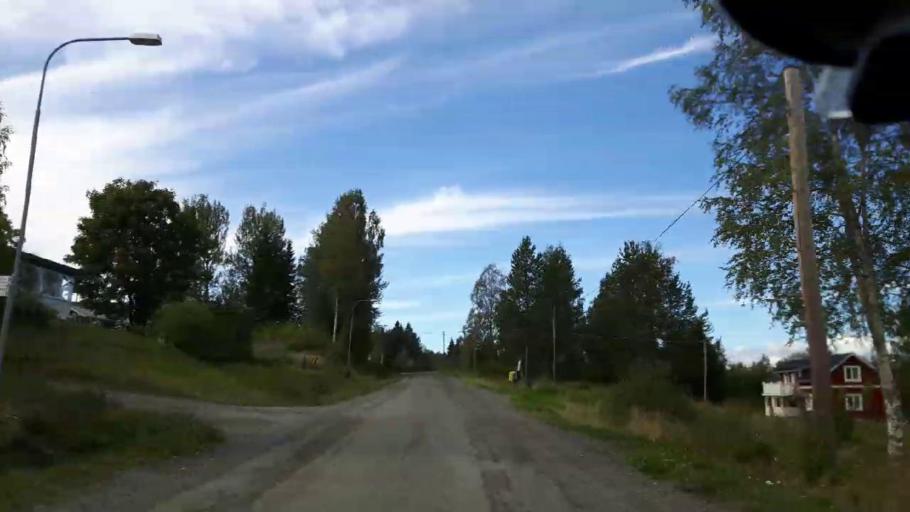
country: SE
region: Jaemtland
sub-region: Ragunda Kommun
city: Hammarstrand
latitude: 63.1361
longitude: 16.2613
